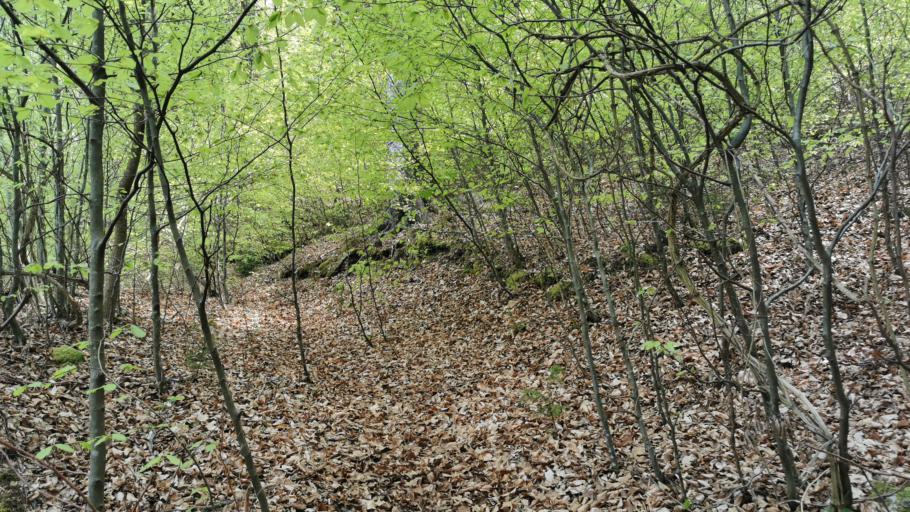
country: AT
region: Salzburg
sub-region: Politischer Bezirk Salzburg-Umgebung
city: Grodig
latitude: 47.7420
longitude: 13.0181
